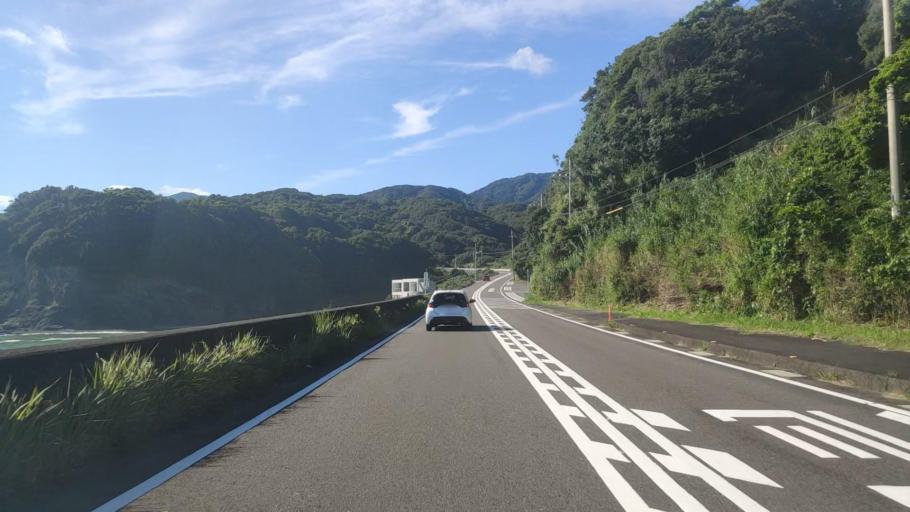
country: JP
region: Wakayama
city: Tanabe
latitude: 33.5043
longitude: 135.6401
